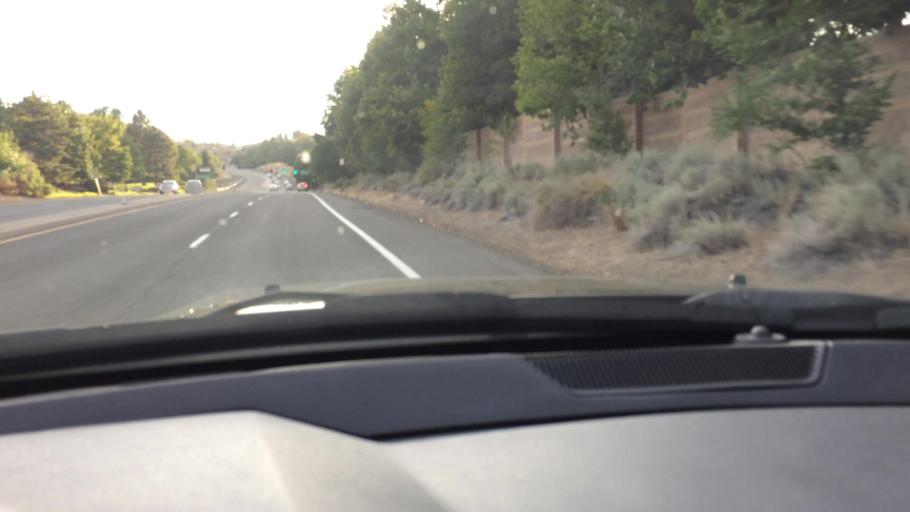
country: US
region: Nevada
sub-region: Washoe County
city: Reno
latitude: 39.4775
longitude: -119.8202
